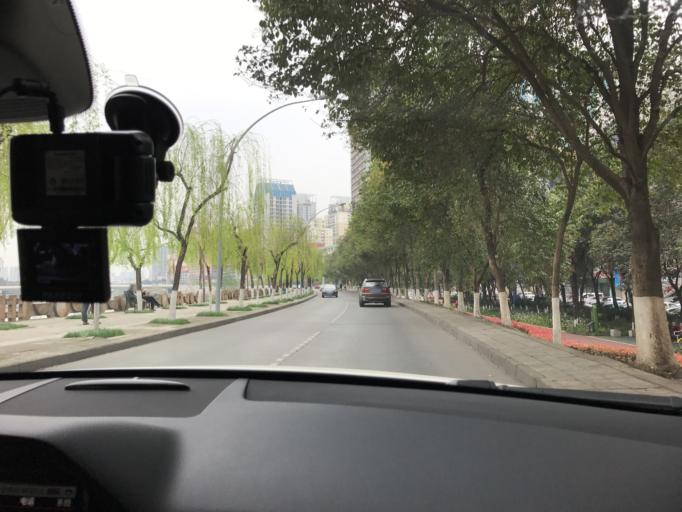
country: CN
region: Sichuan
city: Mianyang
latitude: 31.4617
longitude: 104.7426
